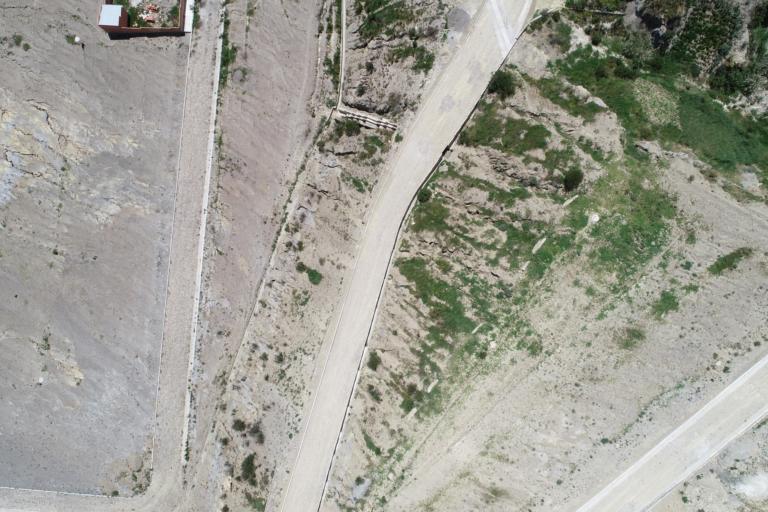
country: BO
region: La Paz
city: La Paz
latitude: -16.5231
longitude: -68.0461
